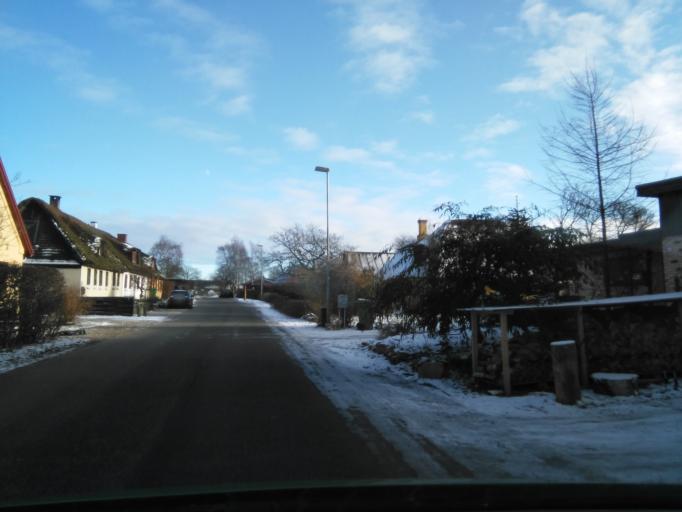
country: DK
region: Central Jutland
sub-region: Skanderborg Kommune
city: Skovby
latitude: 56.1474
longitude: 9.9761
